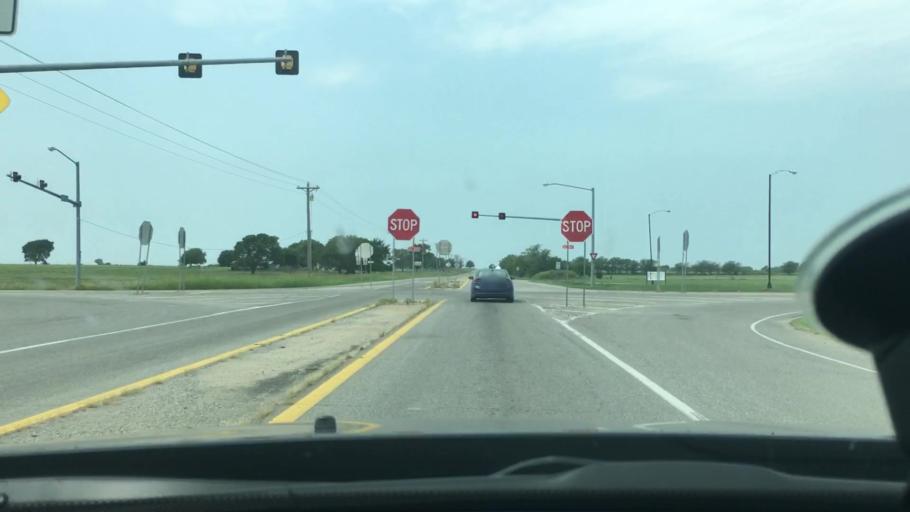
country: US
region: Oklahoma
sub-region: Marshall County
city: Kingston
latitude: 33.9984
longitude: -96.7954
